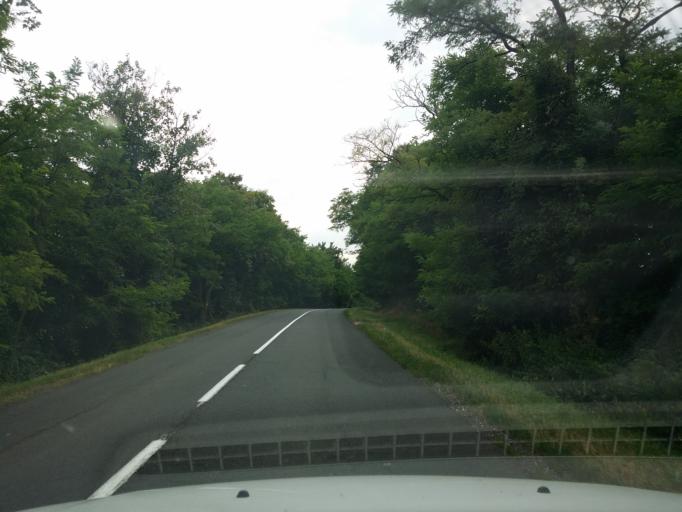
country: HU
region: Nograd
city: Bercel
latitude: 47.9347
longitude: 19.3679
